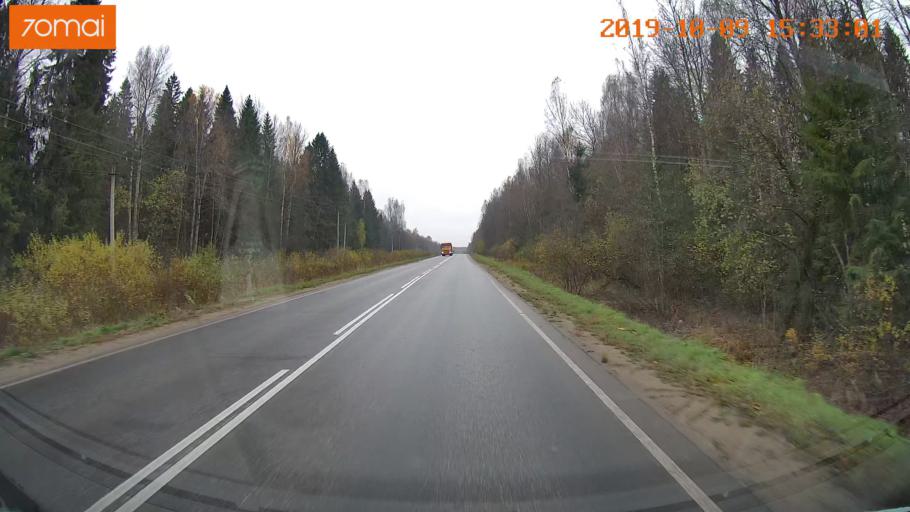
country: RU
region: Kostroma
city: Oktyabr'skiy
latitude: 57.9574
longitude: 41.2681
